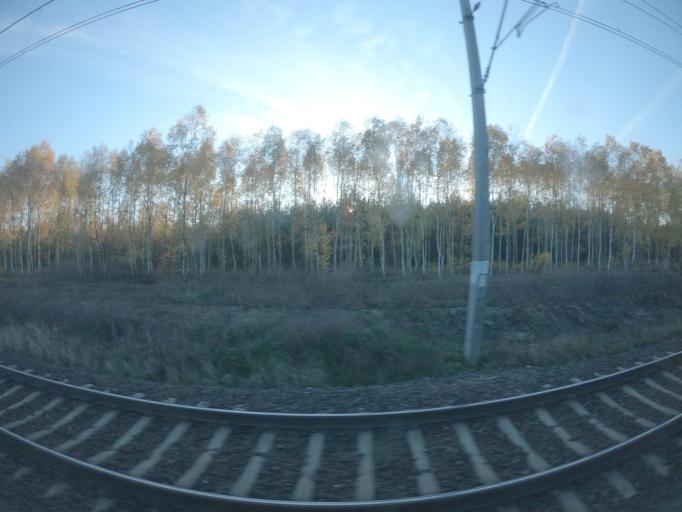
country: PL
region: Lubusz
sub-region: Powiat slubicki
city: Rzepin
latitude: 52.2866
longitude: 14.8950
